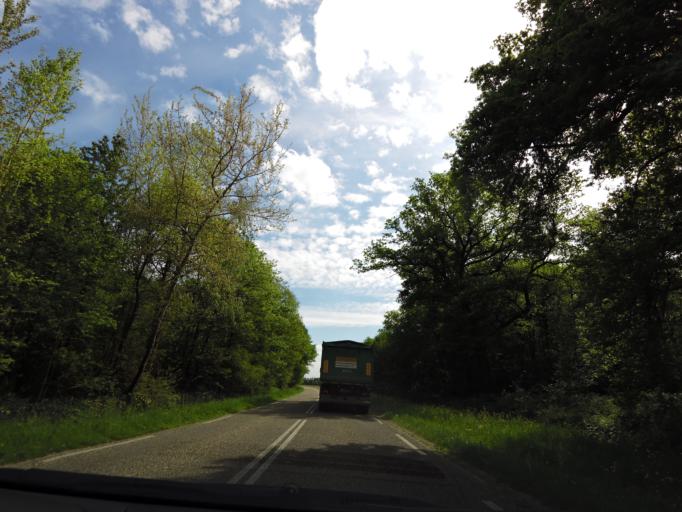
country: NL
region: Limburg
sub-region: Gemeente Leudal
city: Haelen
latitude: 51.2757
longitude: 5.9788
